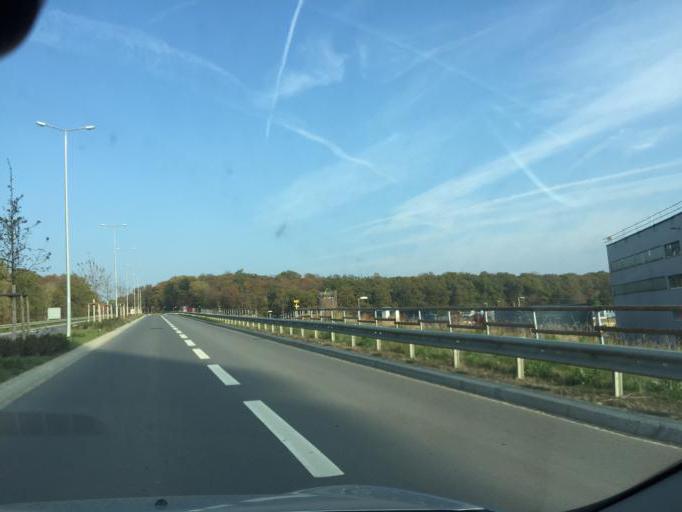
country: LU
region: Luxembourg
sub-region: Canton de Luxembourg
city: Sandweiler
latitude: 49.5973
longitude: 6.2134
